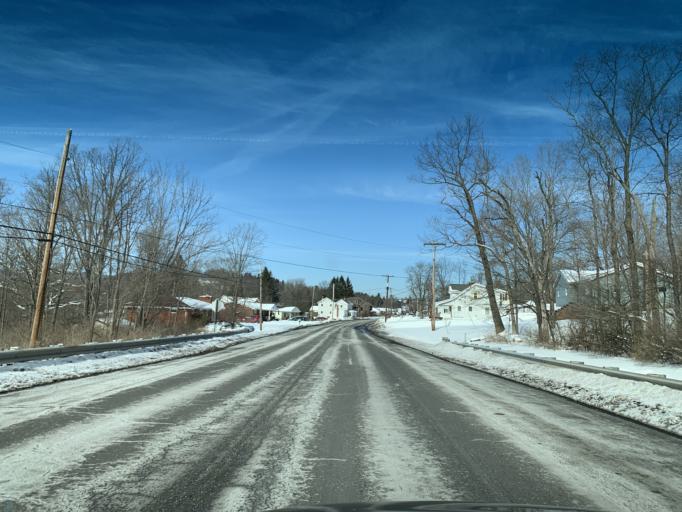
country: US
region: Maryland
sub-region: Allegany County
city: Frostburg
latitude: 39.6357
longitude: -78.9315
